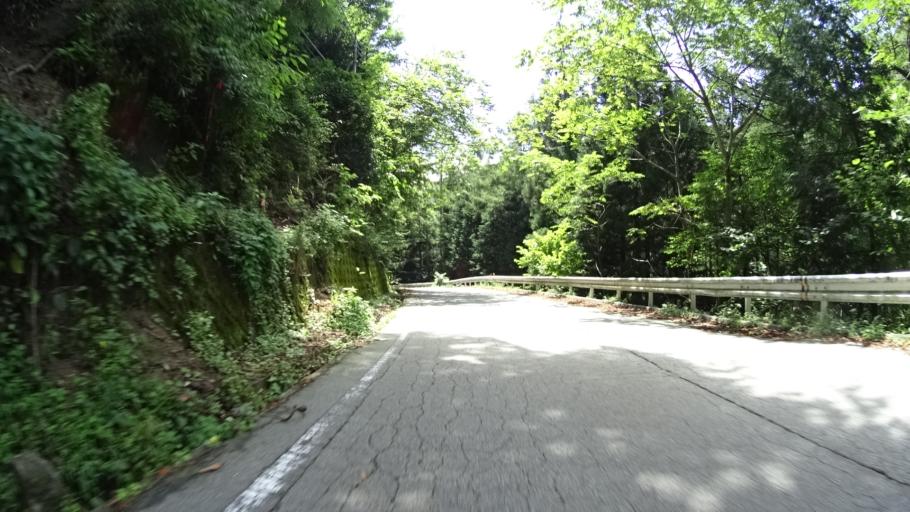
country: JP
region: Yamanashi
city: Enzan
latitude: 35.6644
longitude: 138.8075
